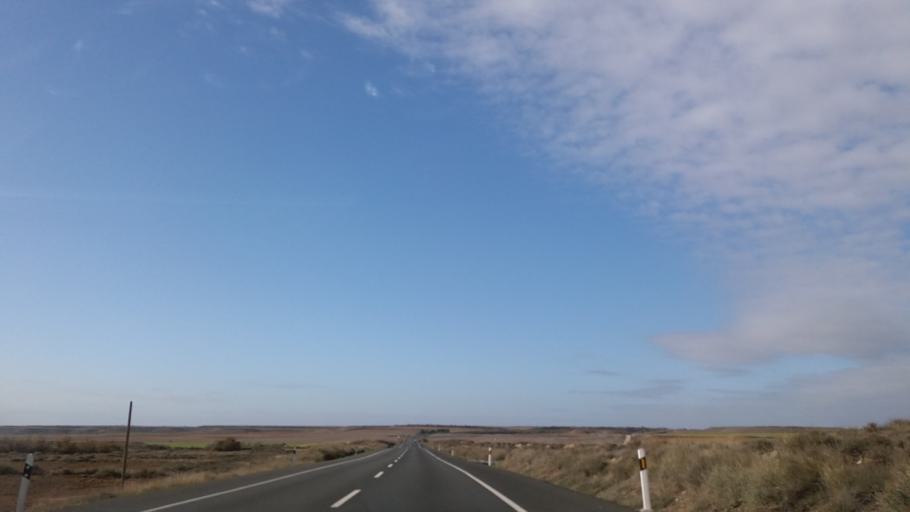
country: ES
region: Aragon
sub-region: Provincia de Huesca
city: Candasnos
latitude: 41.5180
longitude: 0.1629
